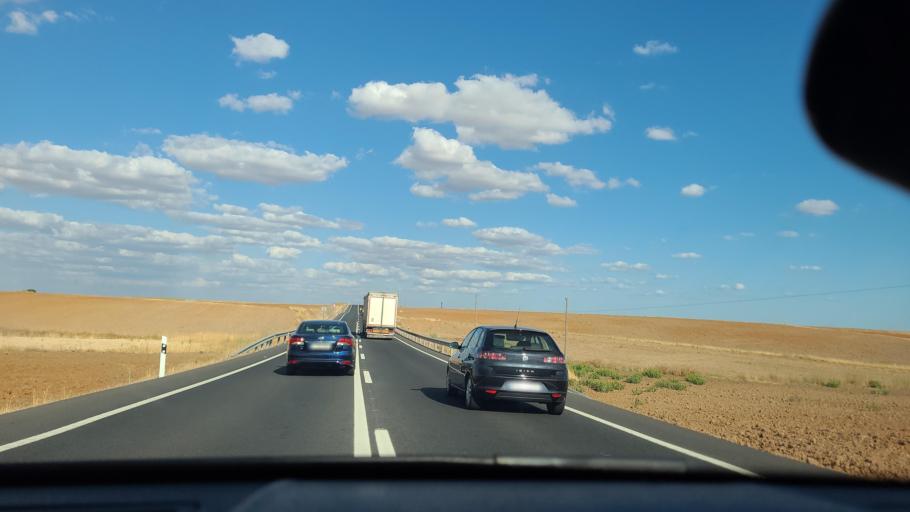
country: ES
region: Extremadura
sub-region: Provincia de Badajoz
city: Azuaga
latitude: 38.2649
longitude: -5.7491
